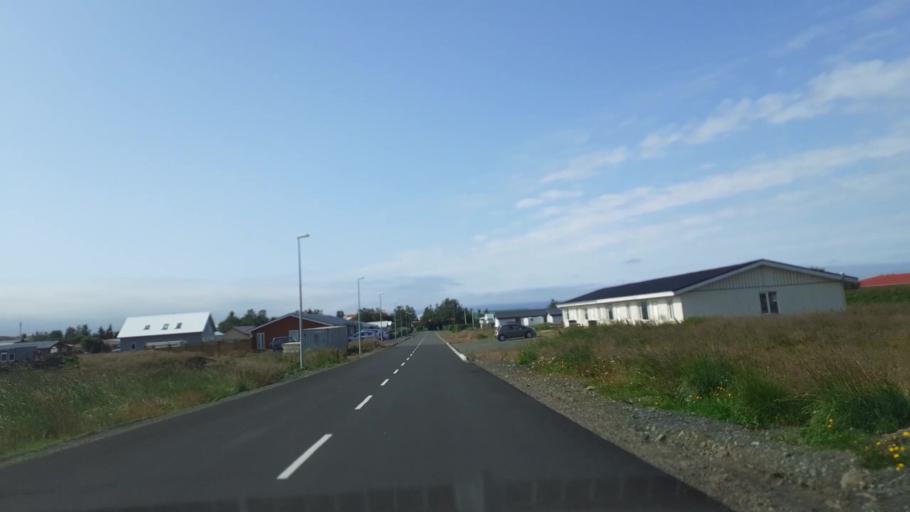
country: IS
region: Northwest
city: Saudarkrokur
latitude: 65.6645
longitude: -20.2850
